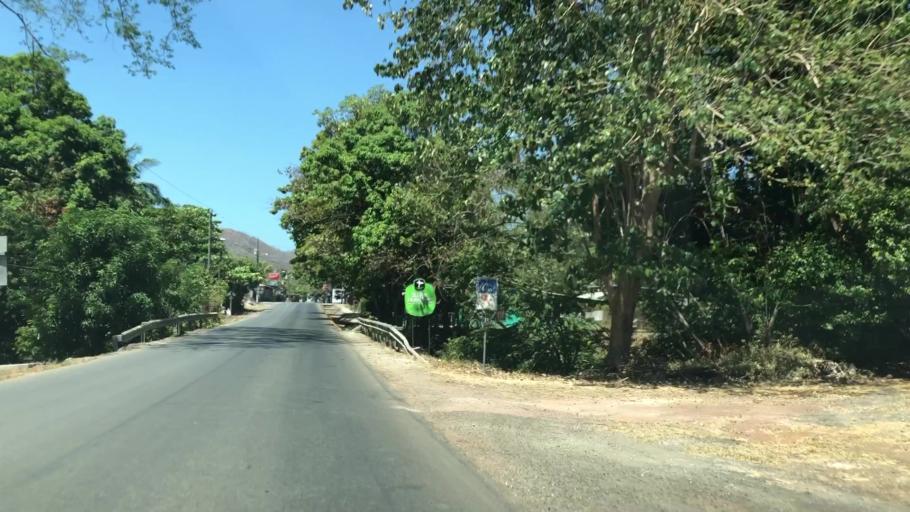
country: CR
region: Guanacaste
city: Sardinal
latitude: 10.3621
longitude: -85.8088
